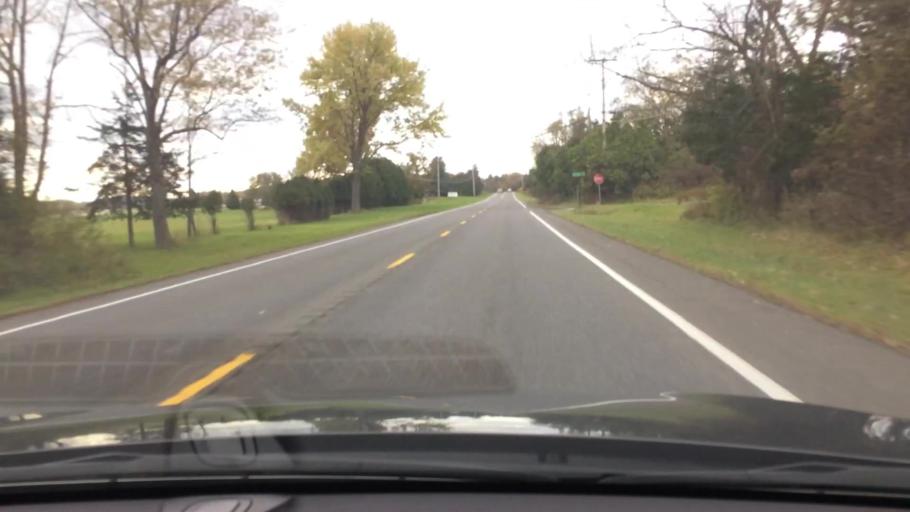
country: US
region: New York
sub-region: Columbia County
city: Stottville
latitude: 42.3044
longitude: -73.7071
